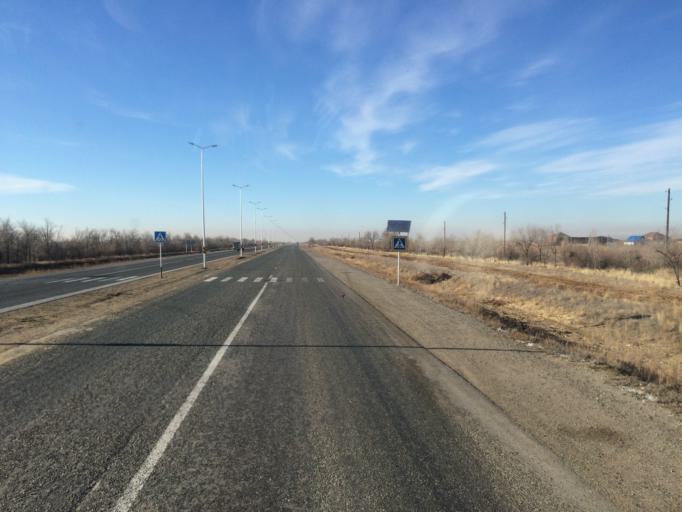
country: KZ
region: Aqtoebe
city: Aqtobe
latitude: 50.2913
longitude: 57.3563
